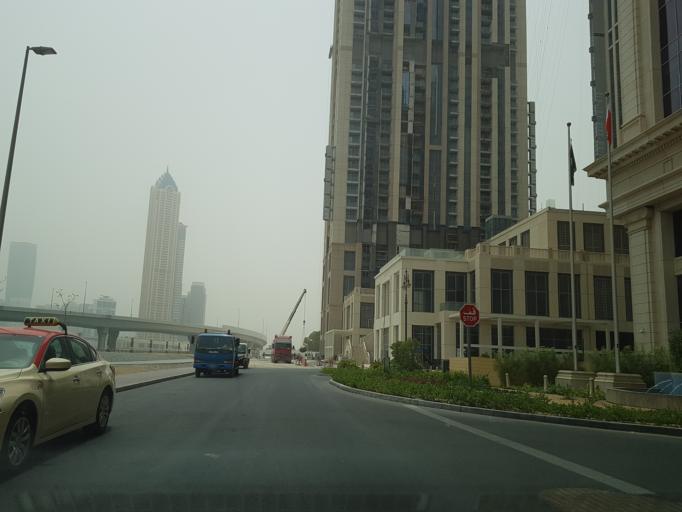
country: AE
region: Dubai
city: Dubai
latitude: 25.1846
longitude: 55.2554
